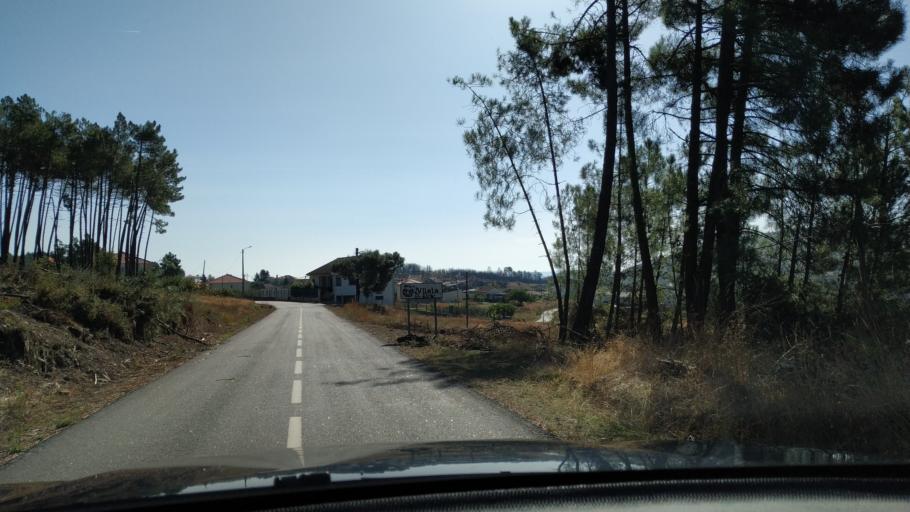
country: PT
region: Vila Real
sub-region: Sabrosa
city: Vilela
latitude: 41.2272
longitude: -7.6076
